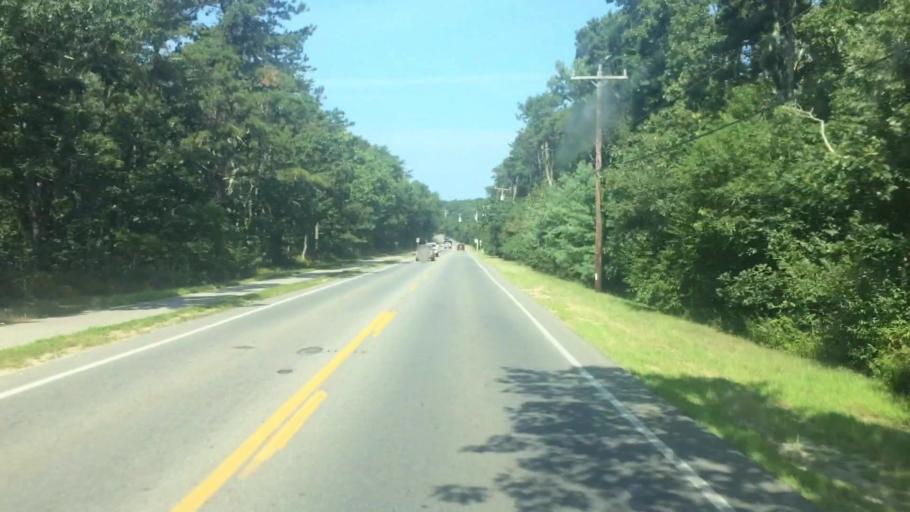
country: US
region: Massachusetts
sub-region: Dukes County
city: Oak Bluffs
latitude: 41.4125
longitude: -70.5759
